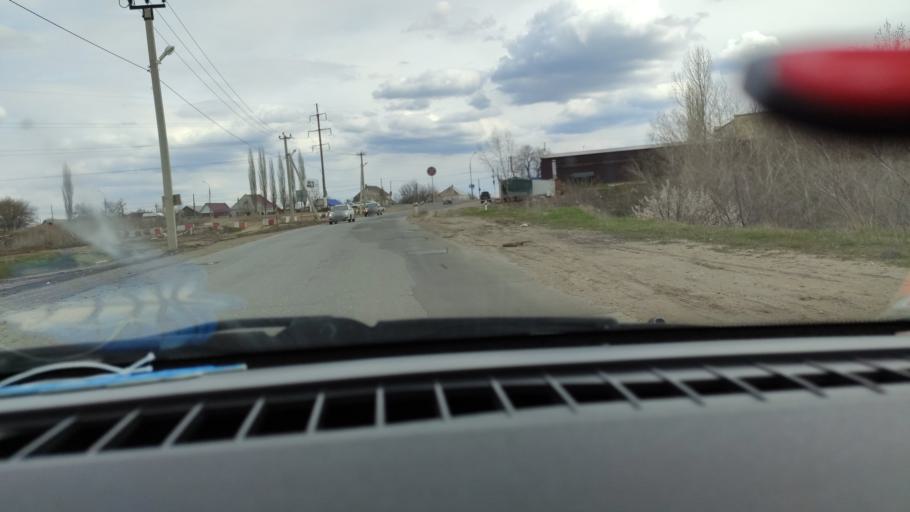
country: RU
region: Saratov
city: Engel's
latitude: 51.4597
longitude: 46.0904
